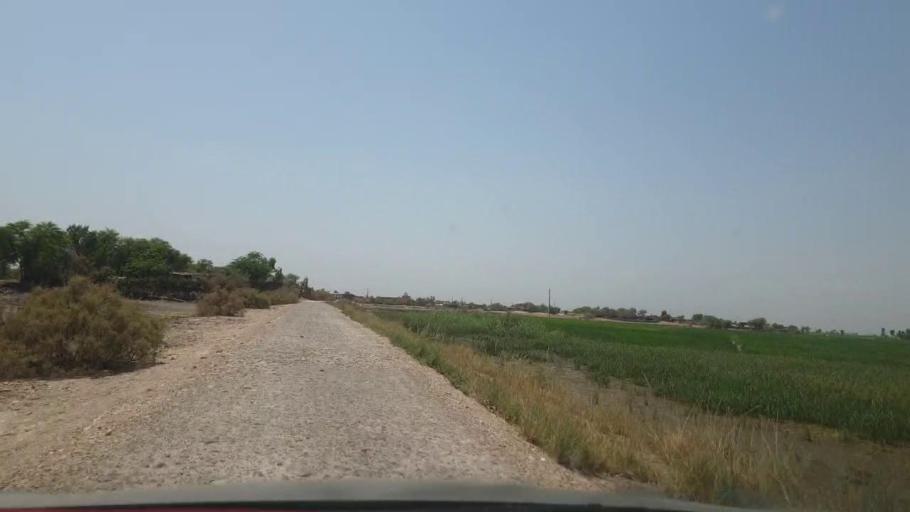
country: PK
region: Sindh
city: Warah
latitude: 27.4854
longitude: 67.7340
